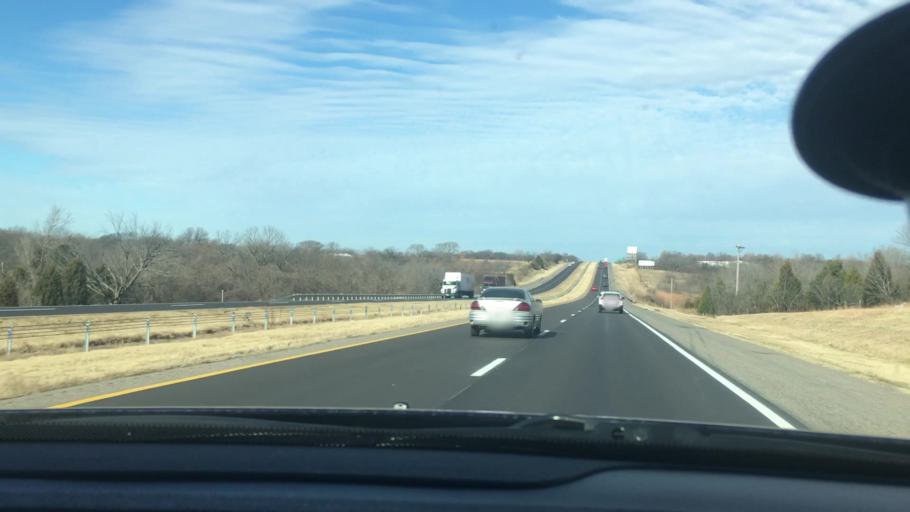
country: US
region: Oklahoma
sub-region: Cleveland County
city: Noble
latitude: 35.1010
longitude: -97.4284
